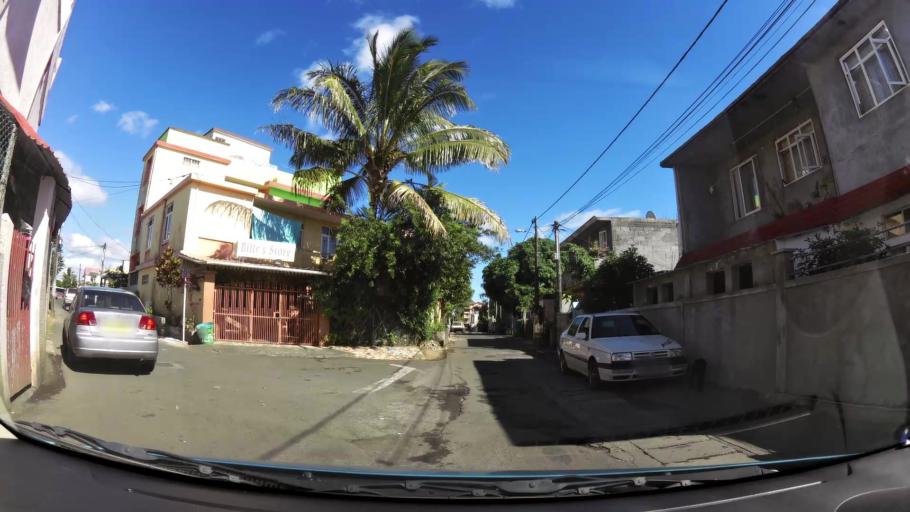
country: MU
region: Plaines Wilhems
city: Quatre Bornes
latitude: -20.2792
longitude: 57.4742
